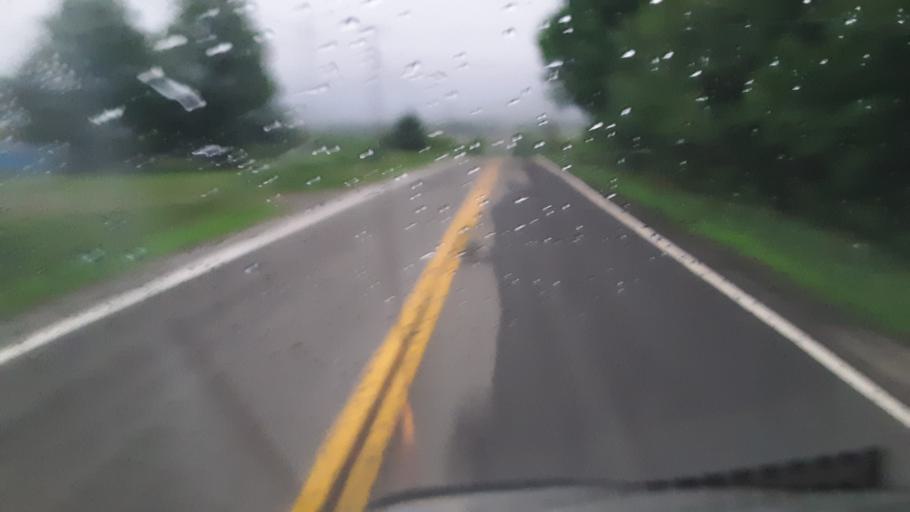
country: US
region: Maine
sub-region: Penobscot County
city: Patten
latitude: 46.0277
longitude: -68.4450
